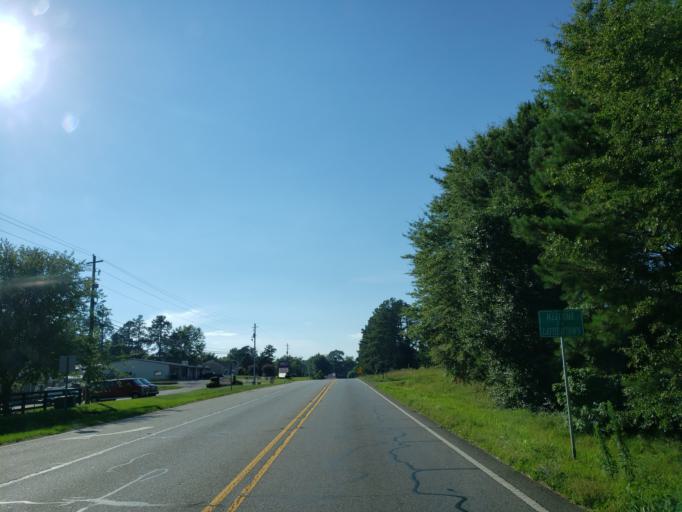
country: US
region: Georgia
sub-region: Fulton County
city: Milton
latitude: 34.2434
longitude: -84.2973
